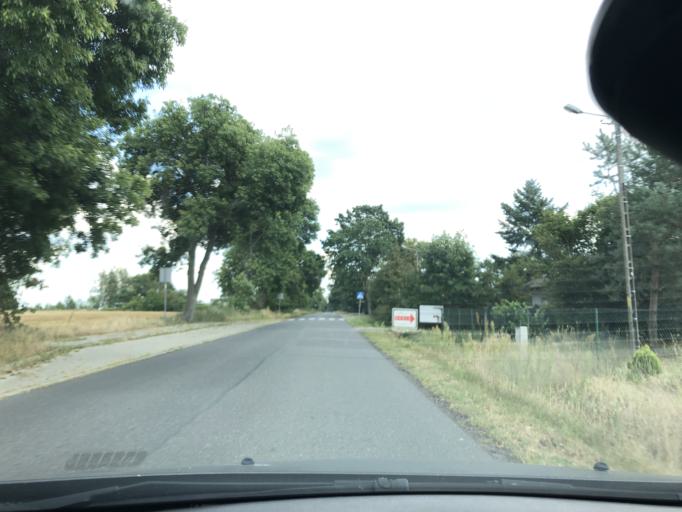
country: PL
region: Lodz Voivodeship
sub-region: Powiat wieruszowski
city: Czastary
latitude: 51.2409
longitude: 18.3690
